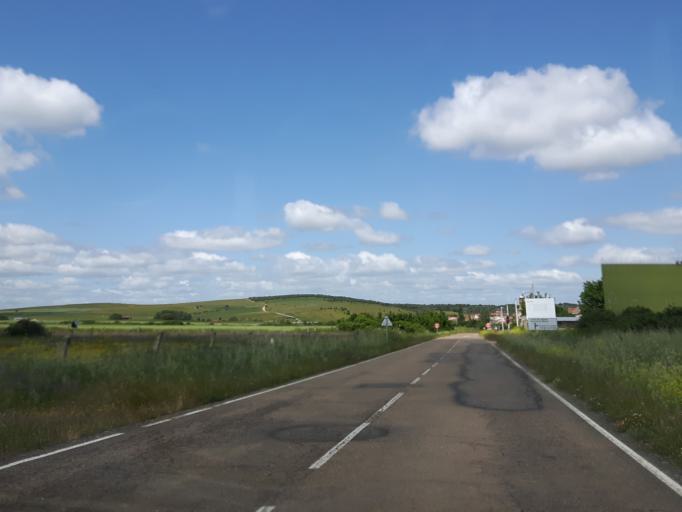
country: ES
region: Castille and Leon
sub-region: Provincia de Salamanca
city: Villar de Ciervo
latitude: 40.7346
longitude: -6.7301
